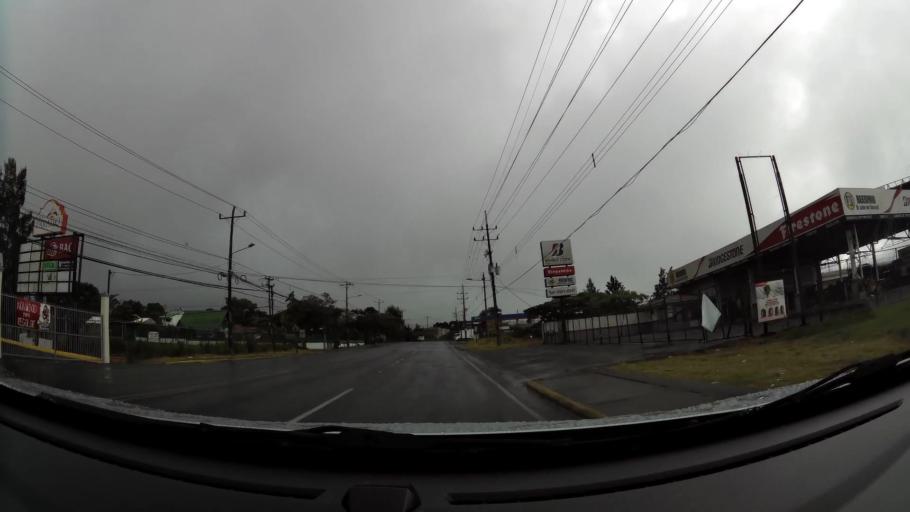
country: CR
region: Cartago
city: Paraiso
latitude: 9.8458
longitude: -83.8913
